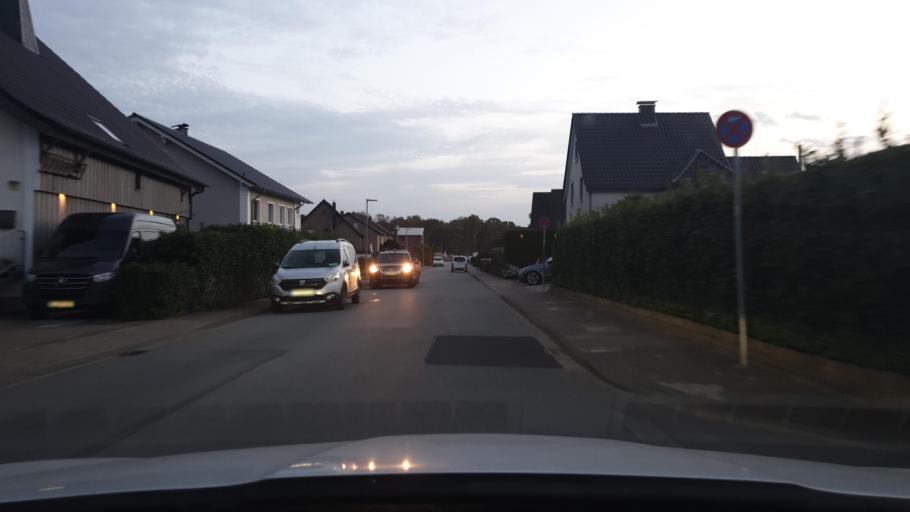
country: DE
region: North Rhine-Westphalia
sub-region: Regierungsbezirk Detmold
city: Bielefeld
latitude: 52.0699
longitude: 8.5798
